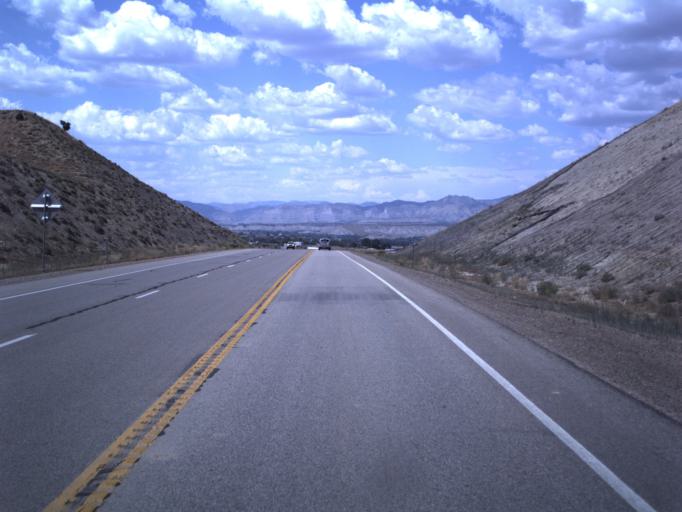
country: US
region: Utah
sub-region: Carbon County
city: Price
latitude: 39.5431
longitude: -110.8147
